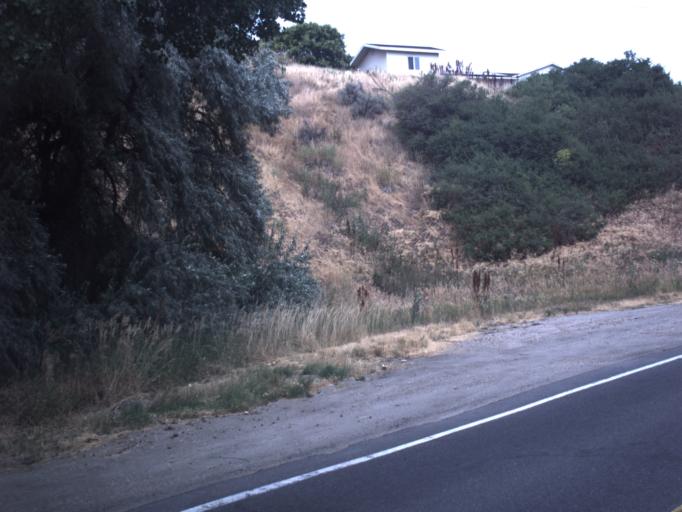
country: US
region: Utah
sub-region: Weber County
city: Riverdale
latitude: 41.1560
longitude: -111.9985
